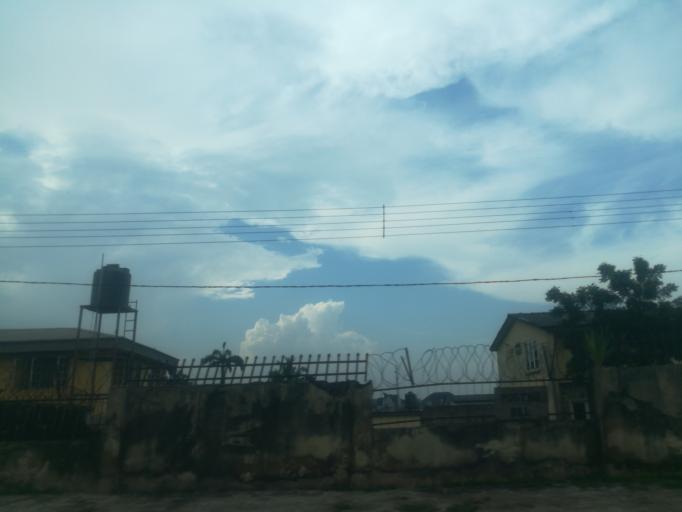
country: NG
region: Oyo
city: Ibadan
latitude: 7.4209
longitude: 3.9033
